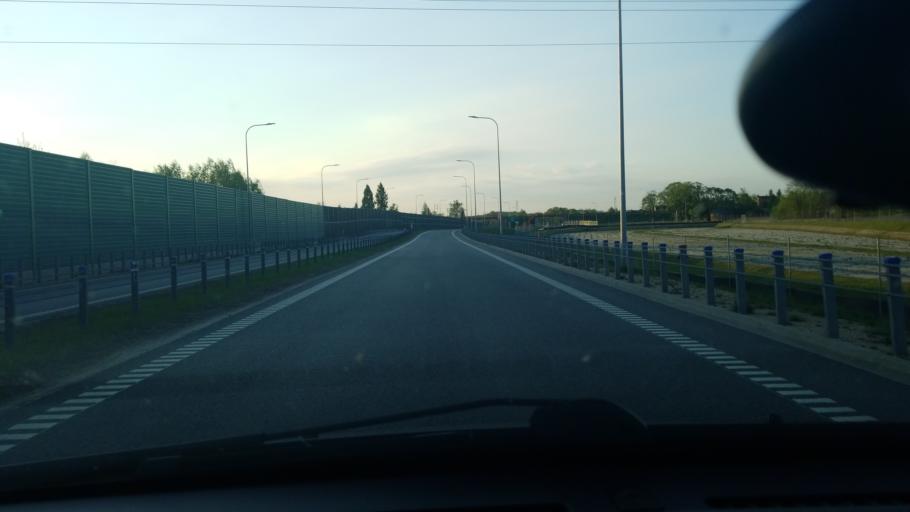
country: PL
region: Silesian Voivodeship
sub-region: Powiat czestochowski
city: Blachownia
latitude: 50.7815
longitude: 19.0112
